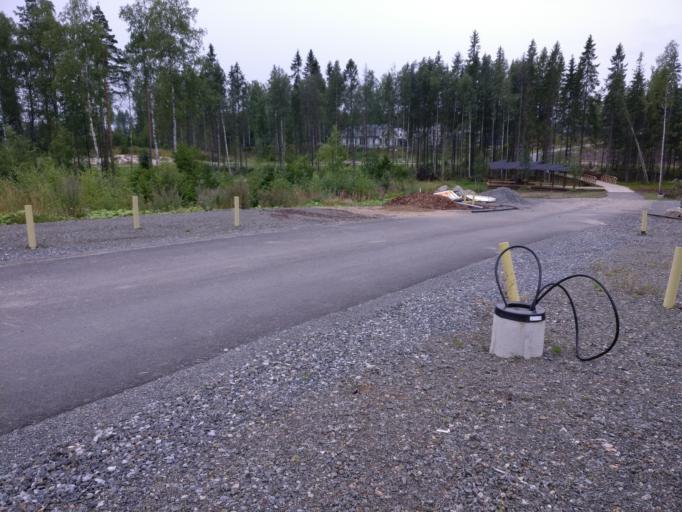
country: FI
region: Pirkanmaa
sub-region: Tampere
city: Tampere
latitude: 61.4405
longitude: 23.8061
